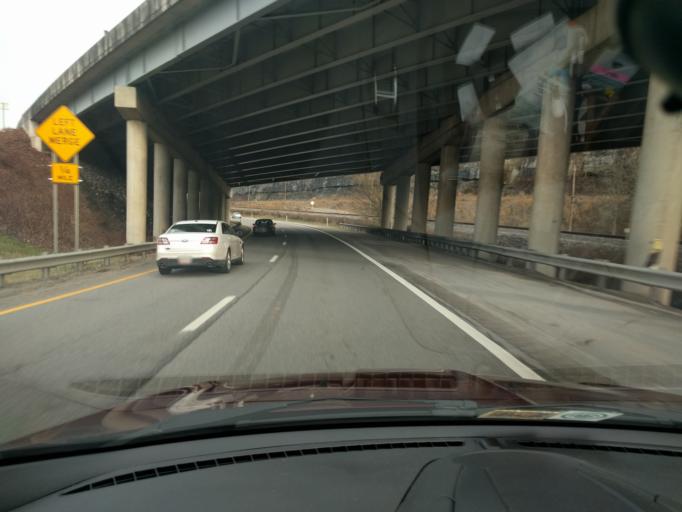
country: US
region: West Virginia
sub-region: Kanawha County
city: Rand
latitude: 38.3175
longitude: -81.5619
